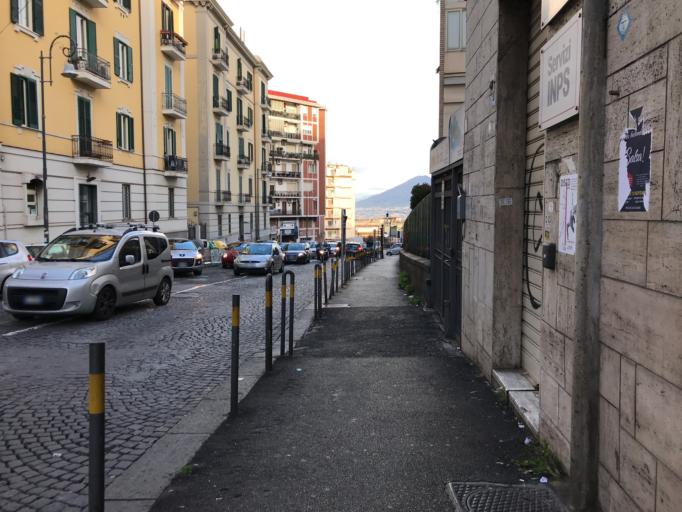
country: IT
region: Campania
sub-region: Provincia di Napoli
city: Napoli
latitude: 40.8536
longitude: 14.2321
